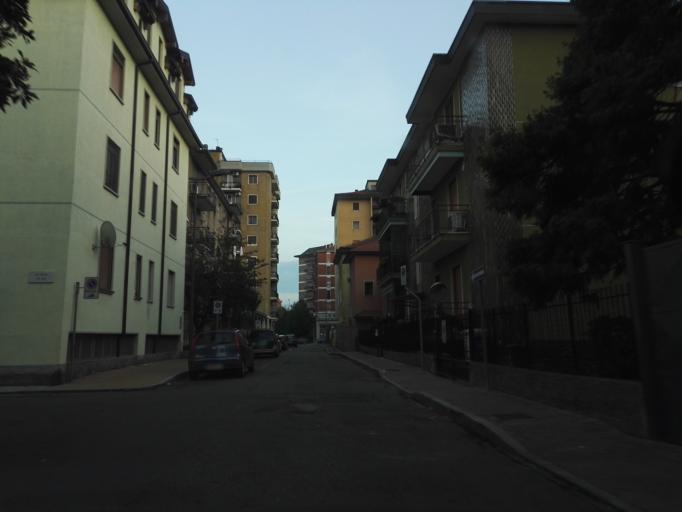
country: IT
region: Lombardy
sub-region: Citta metropolitana di Milano
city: San Giuliano Milanese
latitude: 45.4015
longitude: 9.2802
